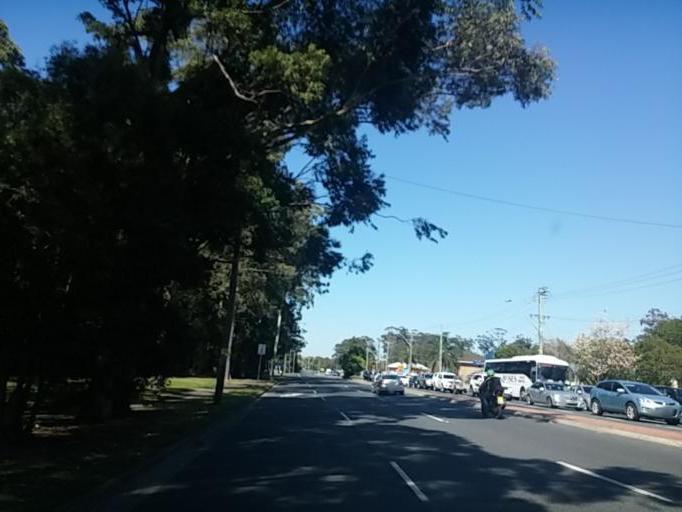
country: AU
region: New South Wales
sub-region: Coffs Harbour
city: Coffs Harbour
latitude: -30.2841
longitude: 153.1266
